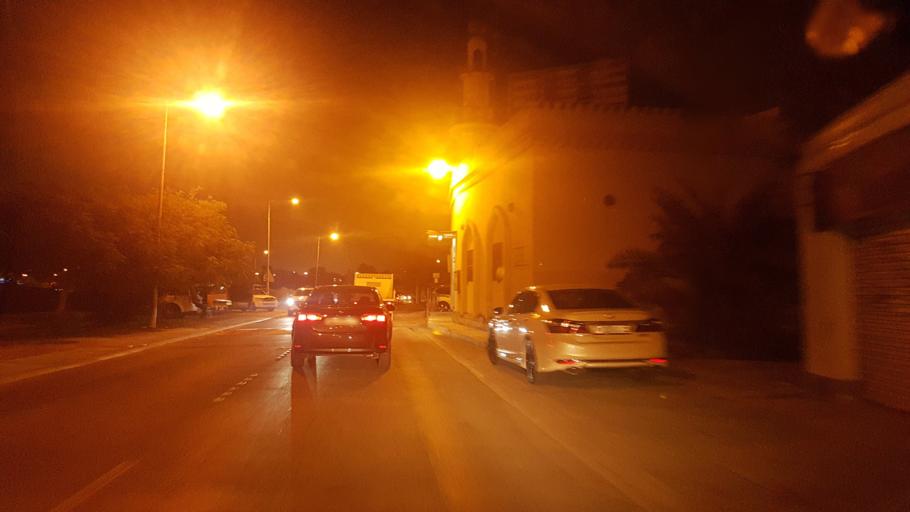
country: BH
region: Manama
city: Jidd Hafs
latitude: 26.2267
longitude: 50.5185
